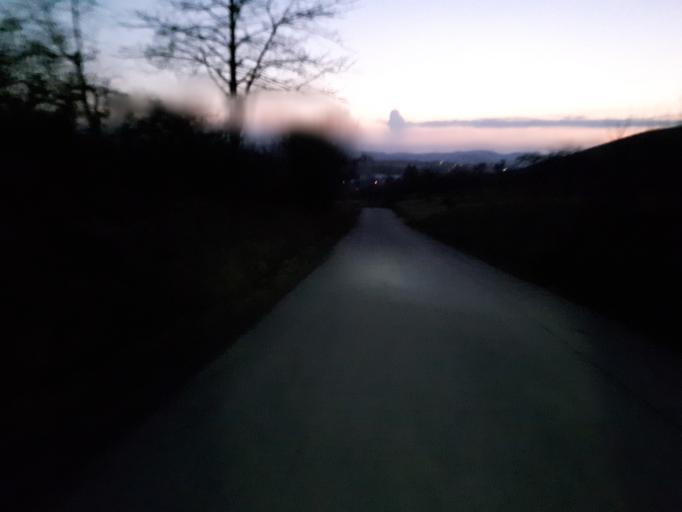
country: DE
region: Baden-Wuerttemberg
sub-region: Regierungsbezirk Stuttgart
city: Bretzfeld
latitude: 49.1443
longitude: 9.4170
